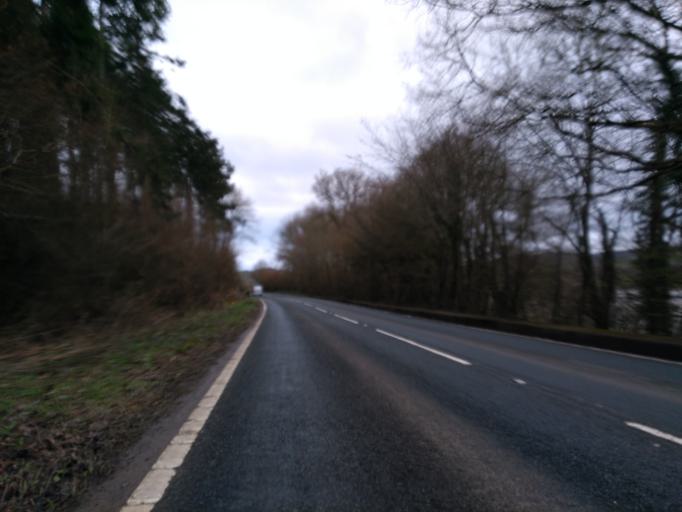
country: GB
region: England
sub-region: Devon
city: Exeter
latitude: 50.7583
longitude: -3.5177
